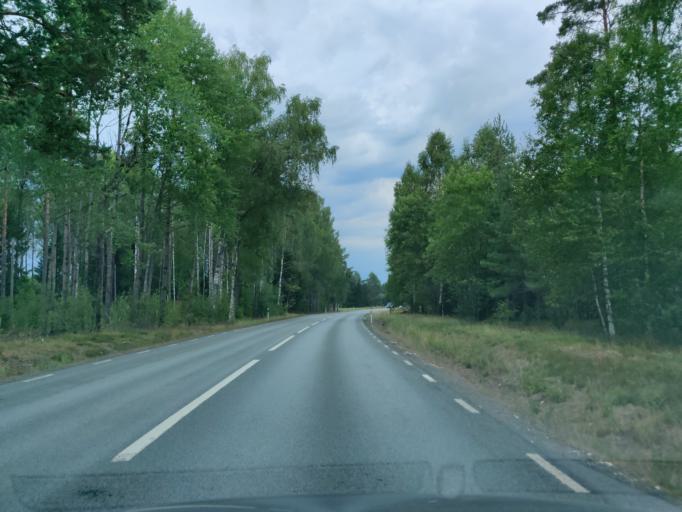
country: SE
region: Vaermland
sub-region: Munkfors Kommun
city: Munkfors
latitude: 59.9618
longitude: 13.5629
